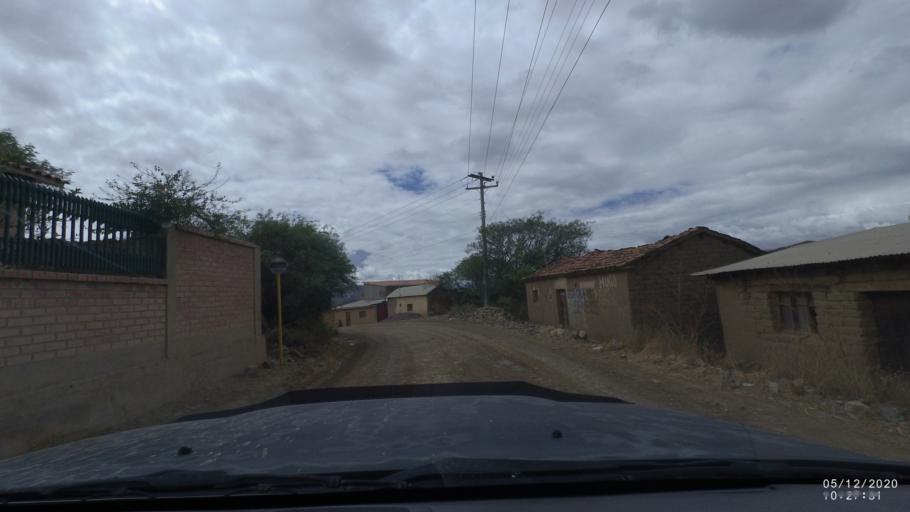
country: BO
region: Cochabamba
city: Sipe Sipe
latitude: -17.5333
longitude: -66.2784
